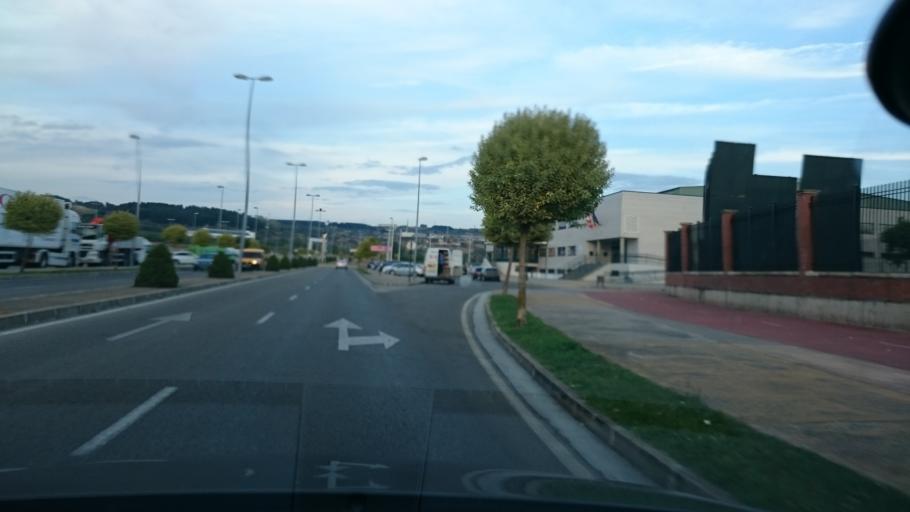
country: ES
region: Castille and Leon
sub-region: Provincia de Leon
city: Ponferrada
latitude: 42.5561
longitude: -6.6003
